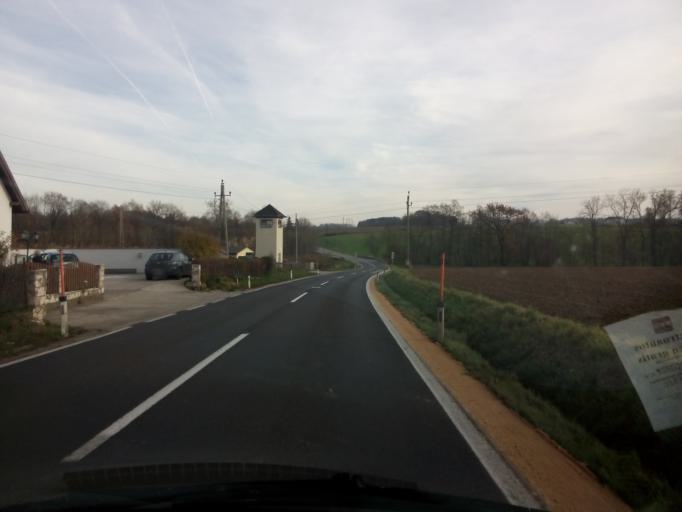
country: AT
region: Upper Austria
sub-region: Wels-Land
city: Sattledt
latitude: 48.0698
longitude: 14.0813
